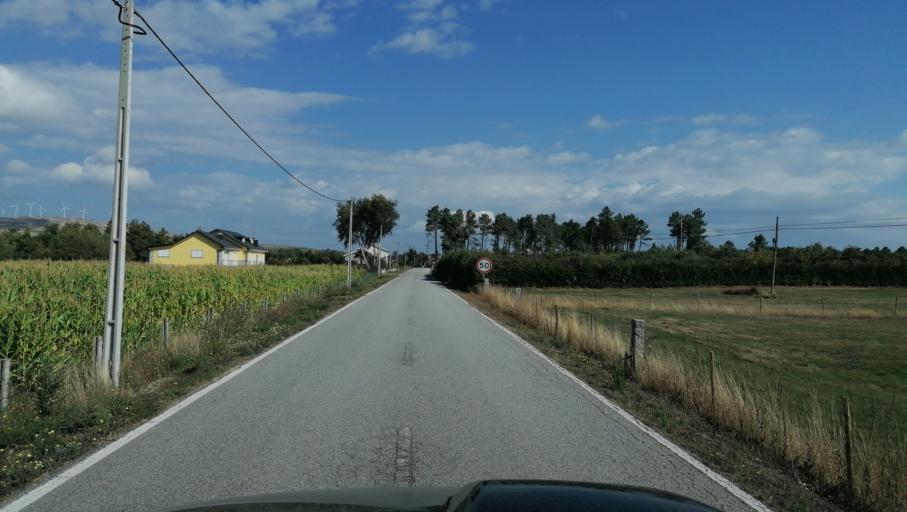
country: PT
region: Vila Real
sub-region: Vila Pouca de Aguiar
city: Vila Pouca de Aguiar
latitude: 41.5097
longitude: -7.6646
